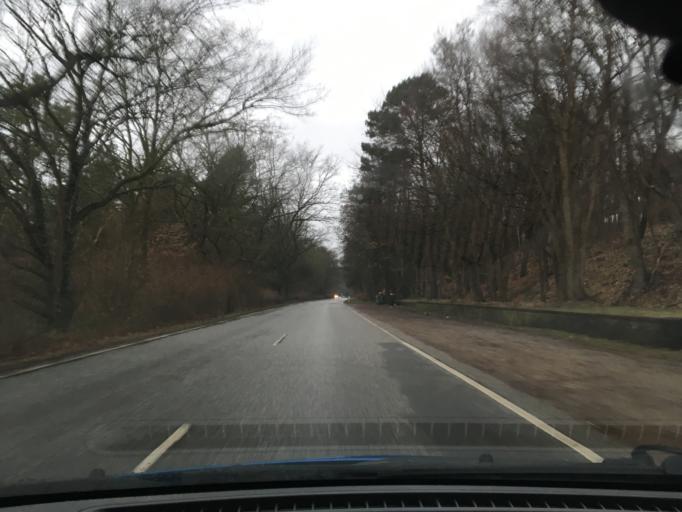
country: DE
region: Lower Saxony
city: Tespe
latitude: 53.4126
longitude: 10.4024
